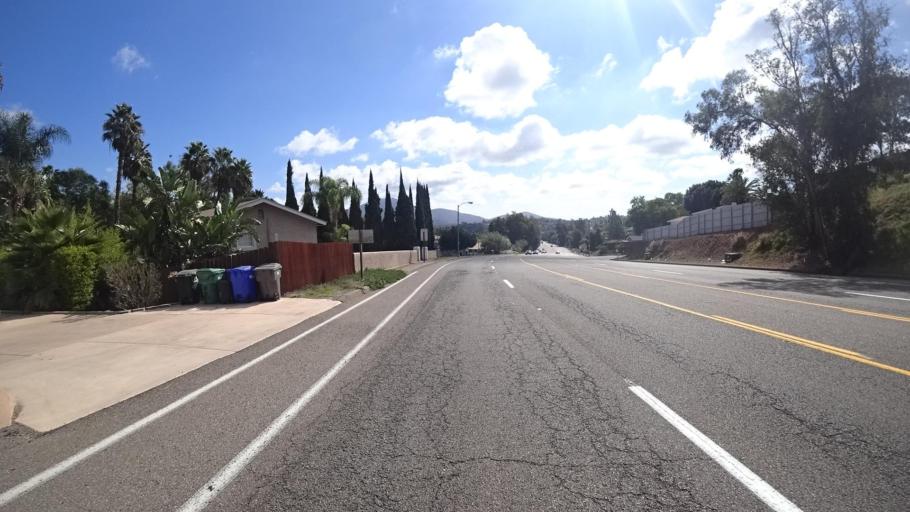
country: US
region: California
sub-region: San Diego County
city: Casa de Oro-Mount Helix
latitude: 32.7562
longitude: -116.9617
